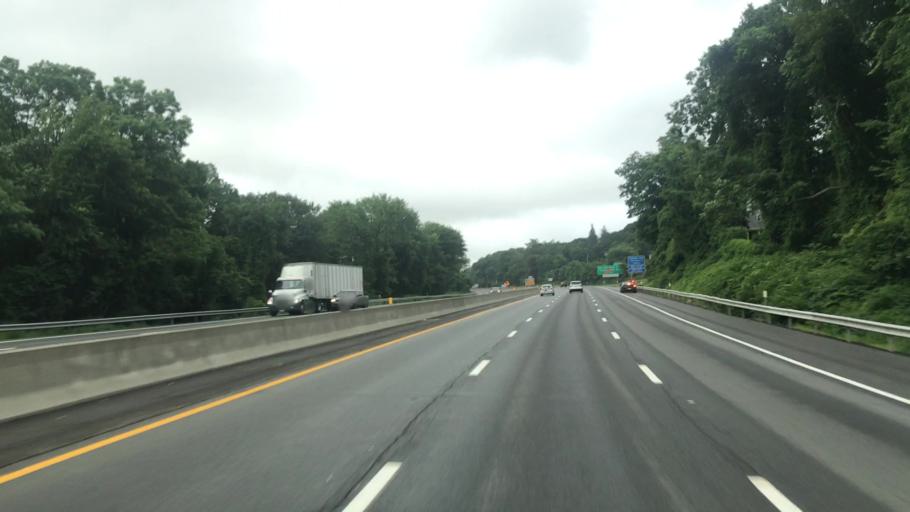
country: US
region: New York
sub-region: Westchester County
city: Greenburgh
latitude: 41.0222
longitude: -73.8452
